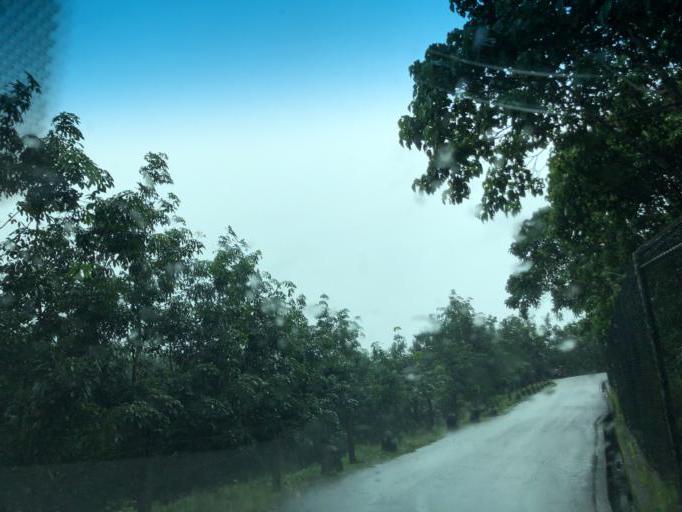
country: LK
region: Western
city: Horana South
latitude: 6.7216
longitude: 80.0611
